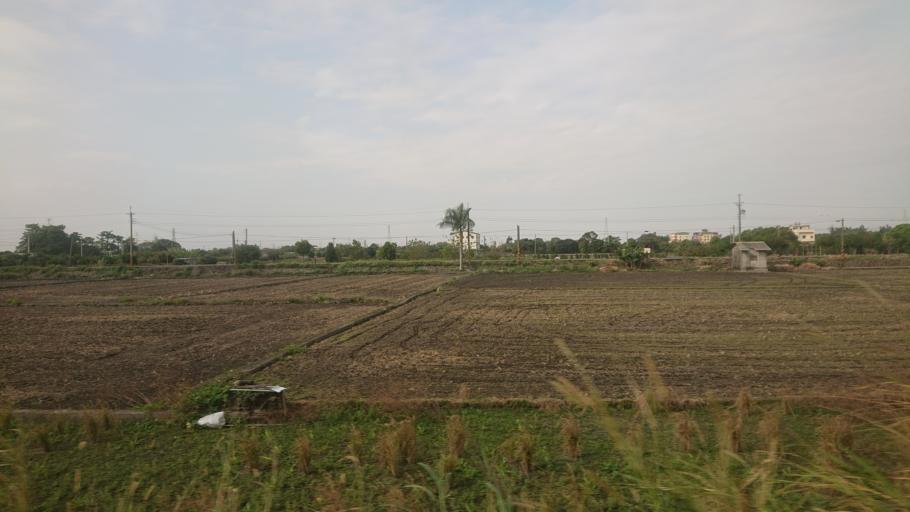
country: TW
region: Taiwan
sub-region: Nantou
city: Nantou
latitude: 23.8908
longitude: 120.5816
